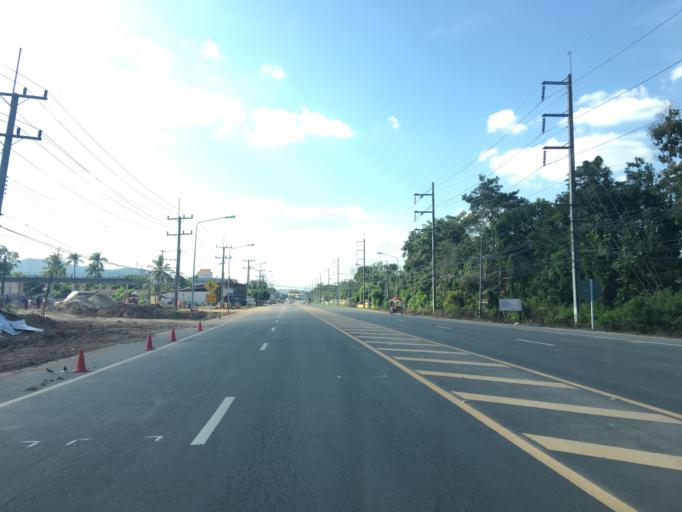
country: TH
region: Phayao
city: Chun
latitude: 19.3345
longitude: 100.1366
